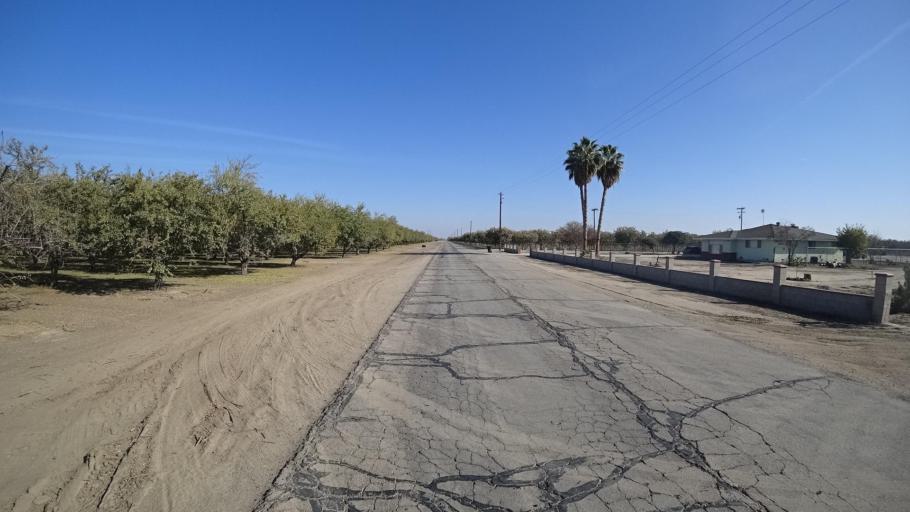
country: US
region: California
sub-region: Kern County
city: Wasco
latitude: 35.6669
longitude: -119.3624
